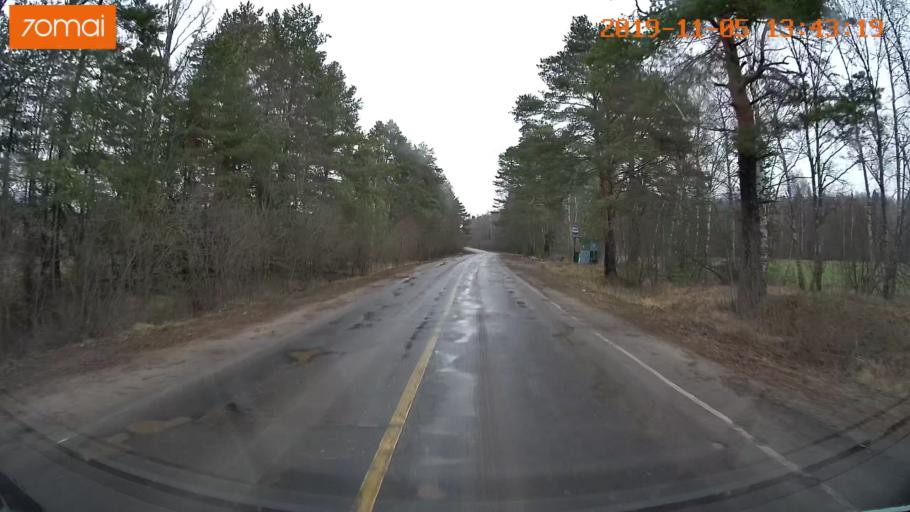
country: RU
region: Ivanovo
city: Shuya
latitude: 56.9727
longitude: 41.4018
